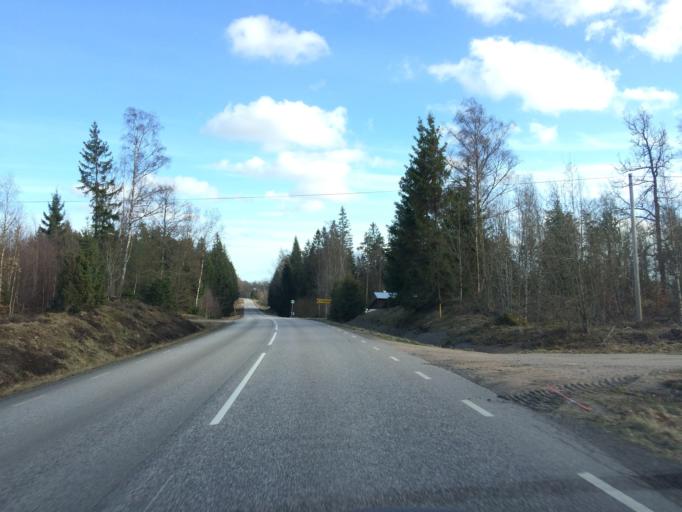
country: SE
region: Kronoberg
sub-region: Almhults Kommun
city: AElmhult
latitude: 56.5794
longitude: 14.1011
